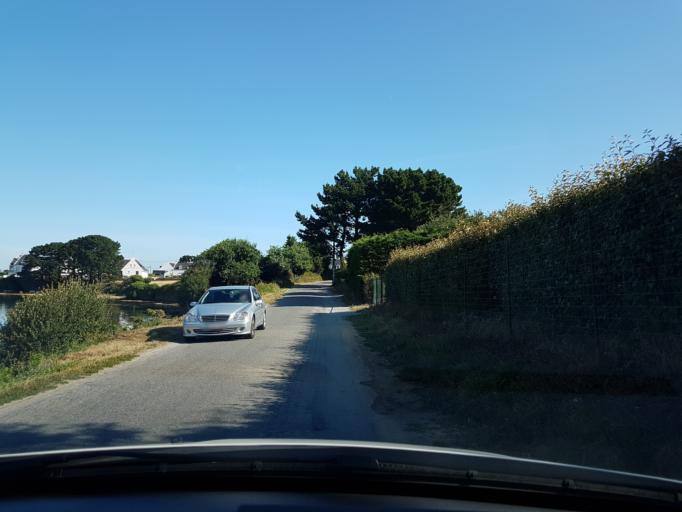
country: FR
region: Brittany
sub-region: Departement du Morbihan
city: Belz
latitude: 47.6790
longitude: -3.1880
